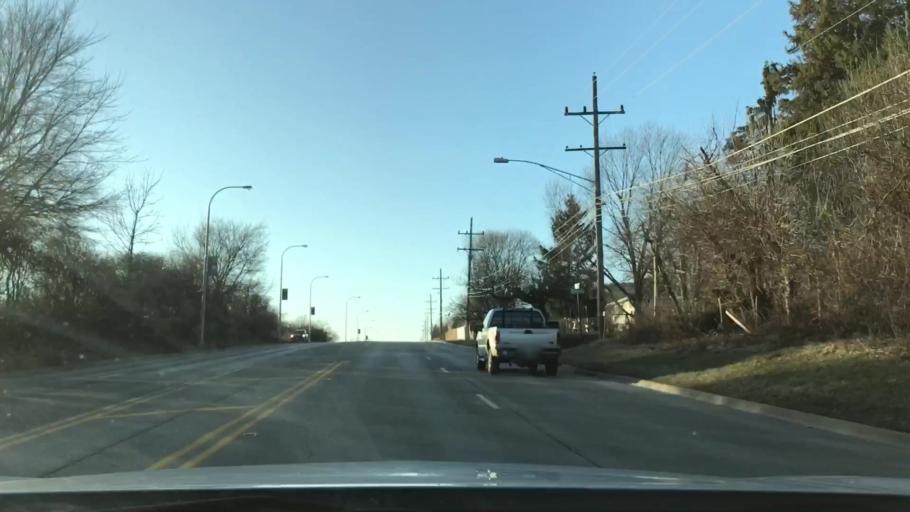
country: US
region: Illinois
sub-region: Kane County
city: Elgin
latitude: 42.0587
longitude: -88.3055
